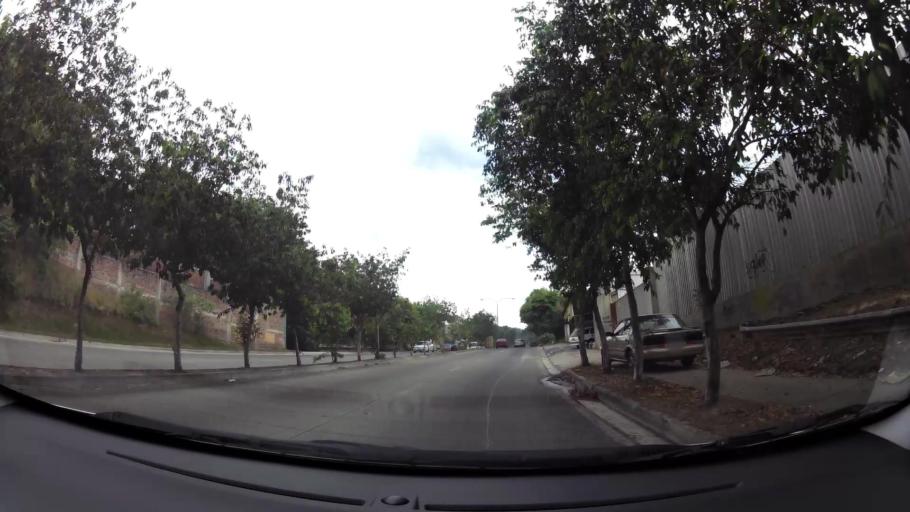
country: SV
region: San Salvador
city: Mejicanos
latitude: 13.7184
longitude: -89.2318
